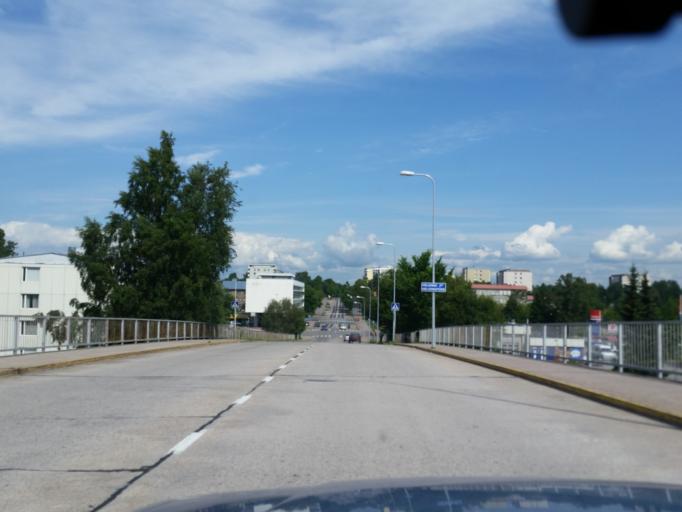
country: FI
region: Uusimaa
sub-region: Raaseporin
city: Hanko
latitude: 59.8265
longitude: 22.9657
